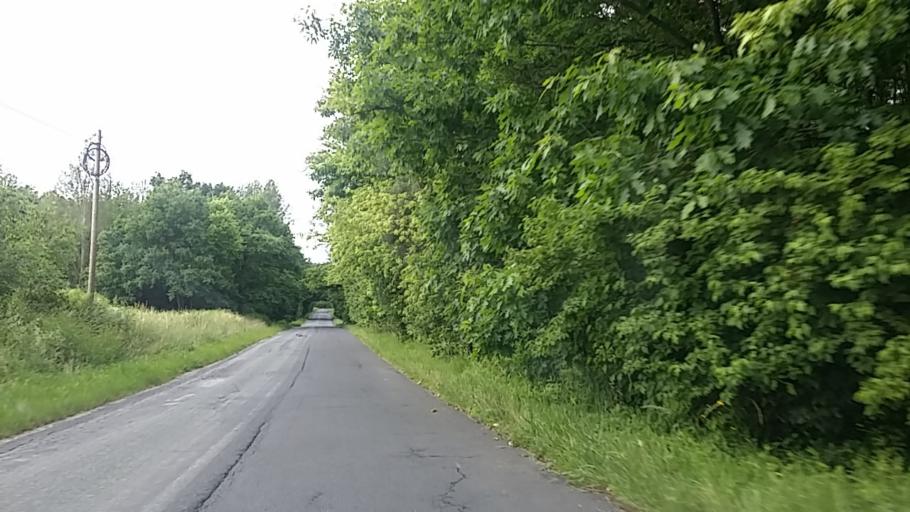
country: HU
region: Zala
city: Zalalovo
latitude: 46.8534
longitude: 16.5022
